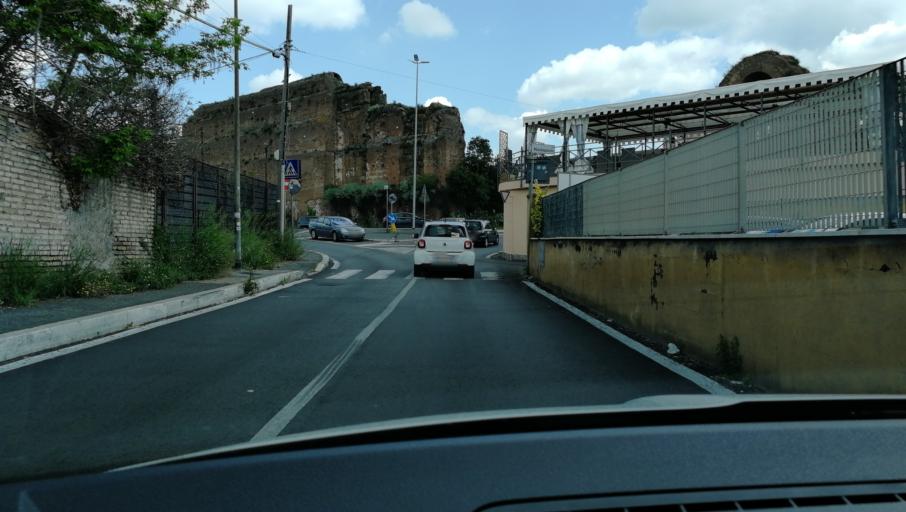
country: IT
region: Latium
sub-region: Citta metropolitana di Roma Capitale
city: Rome
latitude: 41.8642
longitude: 12.5417
